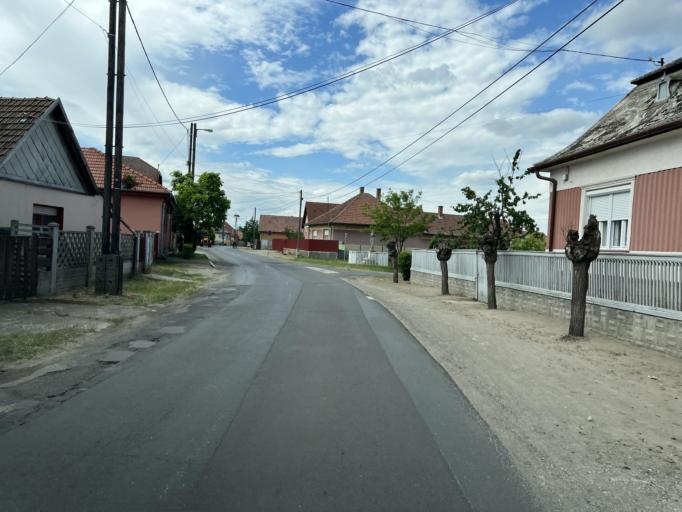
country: HU
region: Pest
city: Szentlorinckata
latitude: 47.5234
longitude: 19.7560
